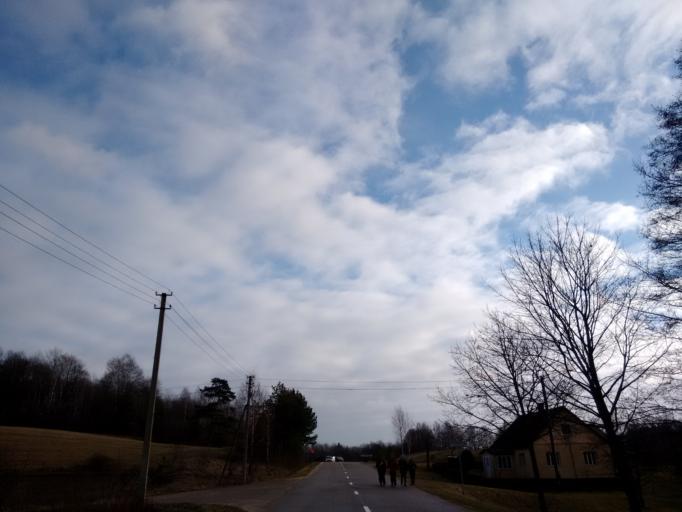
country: LT
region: Alytaus apskritis
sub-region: Alytus
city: Alytus
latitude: 54.2462
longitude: 23.9304
